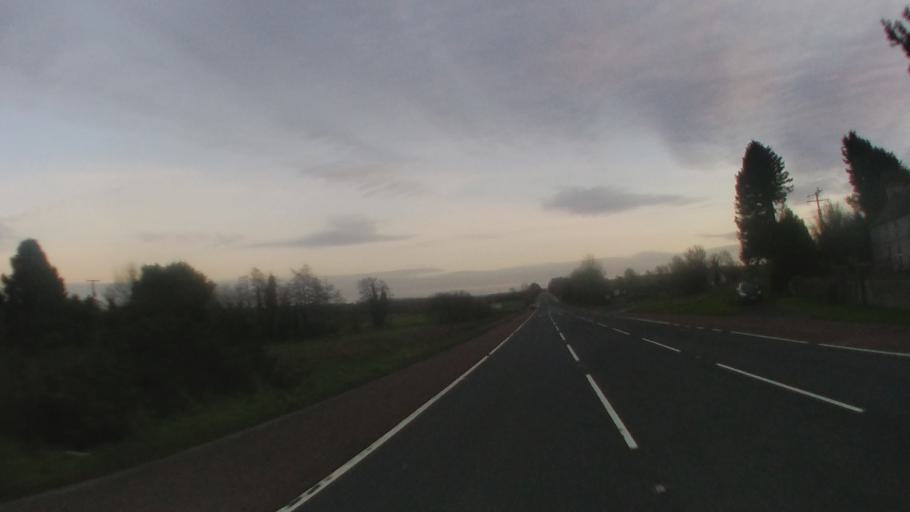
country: GB
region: Northern Ireland
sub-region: Armagh District
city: Tandragee
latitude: 54.2894
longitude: -6.5005
